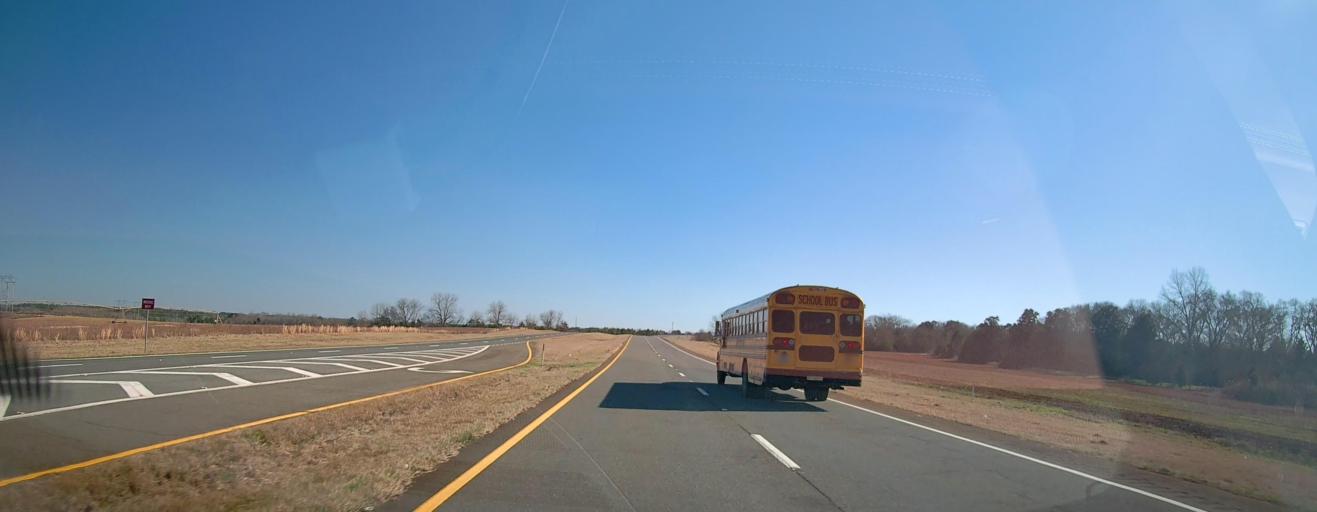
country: US
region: Georgia
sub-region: Sumter County
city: Americus
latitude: 32.1424
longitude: -84.2677
